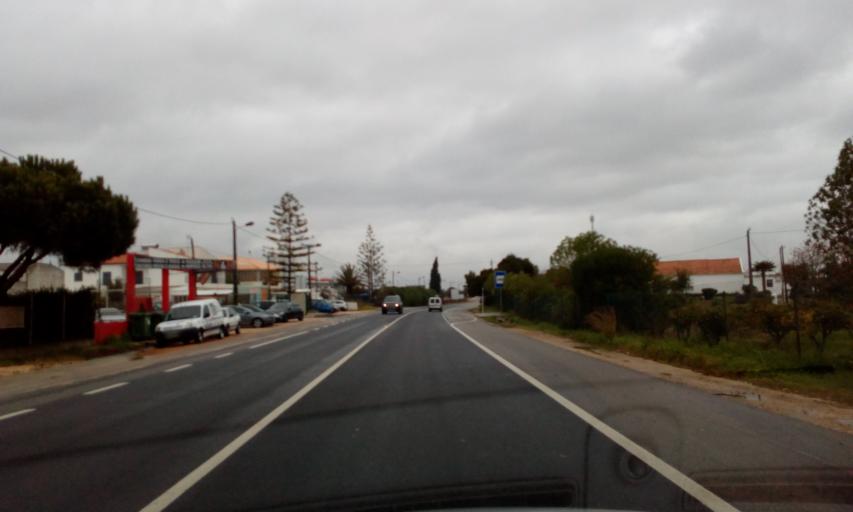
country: PT
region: Faro
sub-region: Lagos
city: Lagos
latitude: 37.1424
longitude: -8.6622
